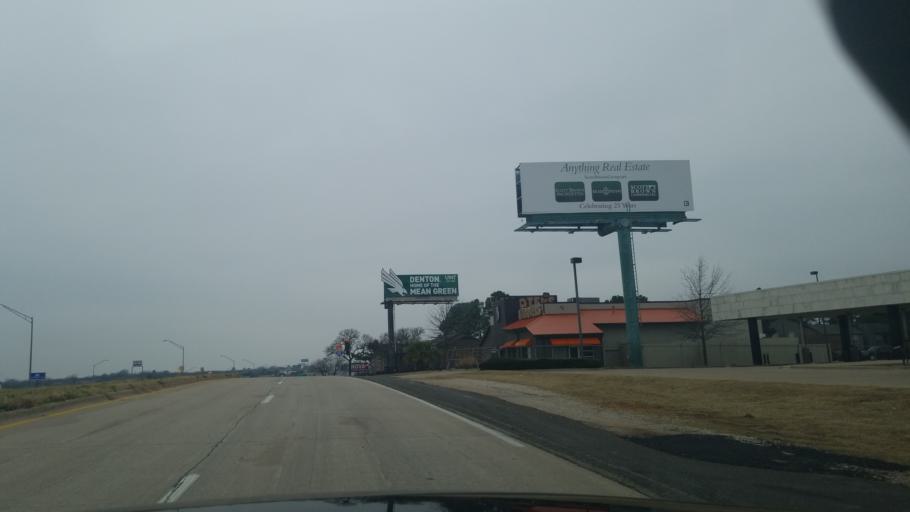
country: US
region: Texas
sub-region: Denton County
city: Denton
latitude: 33.1930
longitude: -97.1188
